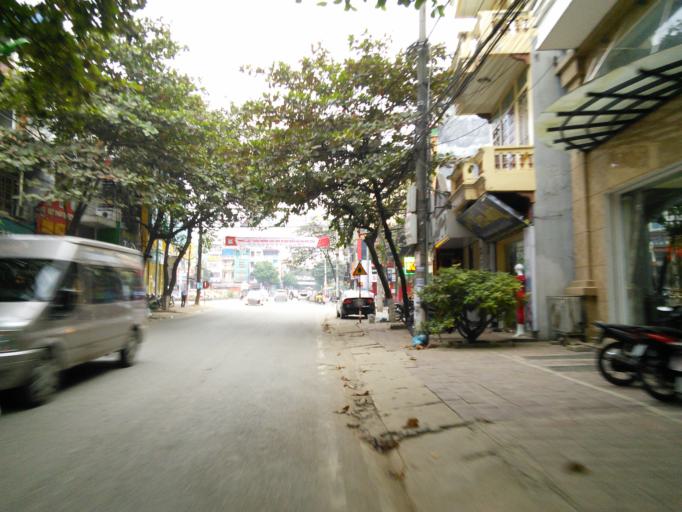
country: VN
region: Lao Cai
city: Lao Cai
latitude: 22.4928
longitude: 103.9770
